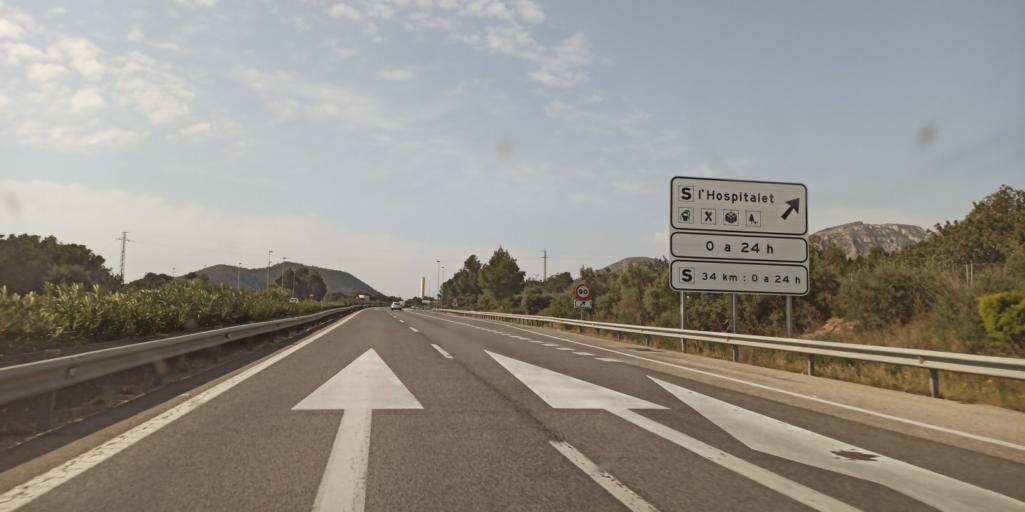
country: ES
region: Catalonia
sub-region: Provincia de Tarragona
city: Colldejou
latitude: 40.9887
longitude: 0.8990
